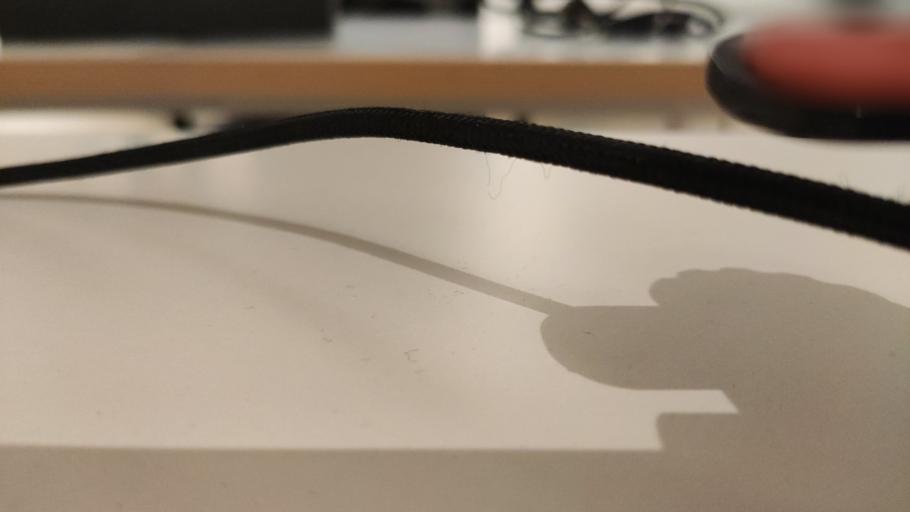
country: RU
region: Moskovskaya
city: Dorokhovo
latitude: 55.3727
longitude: 36.4094
